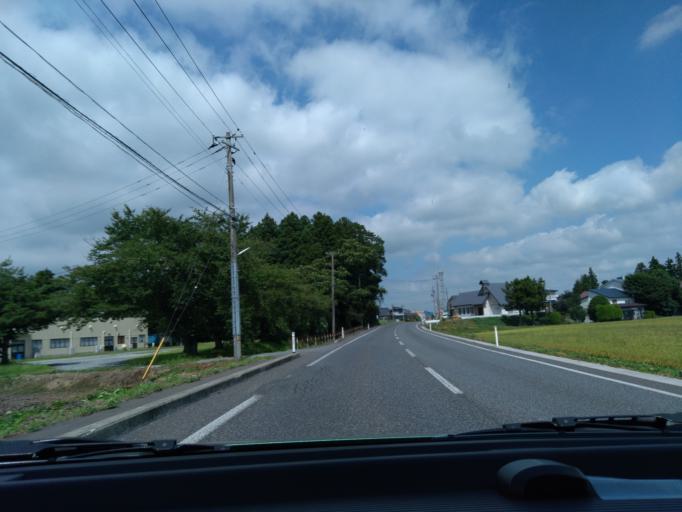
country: JP
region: Iwate
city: Hanamaki
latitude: 39.3847
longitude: 141.0551
